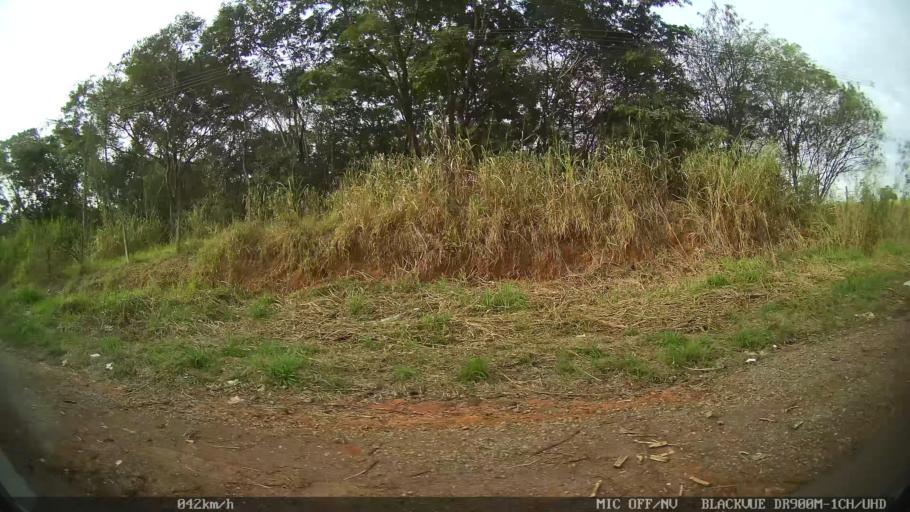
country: BR
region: Sao Paulo
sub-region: Piracicaba
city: Piracicaba
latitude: -22.6909
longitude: -47.5821
